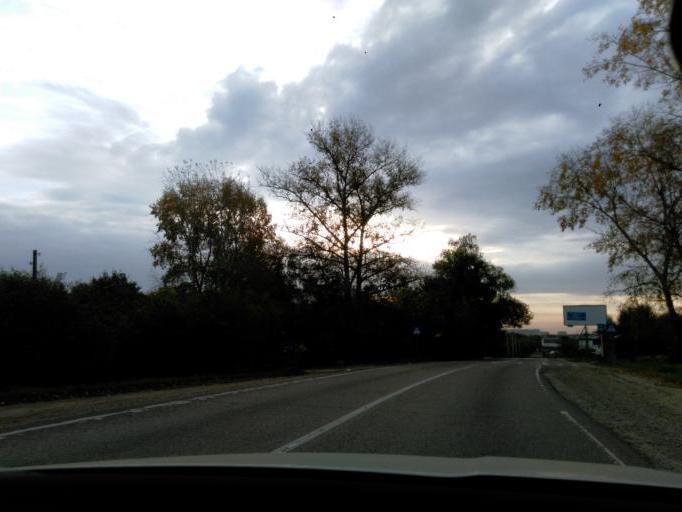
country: RU
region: Moskovskaya
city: Sheremet'yevskiy
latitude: 55.9724
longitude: 37.4665
